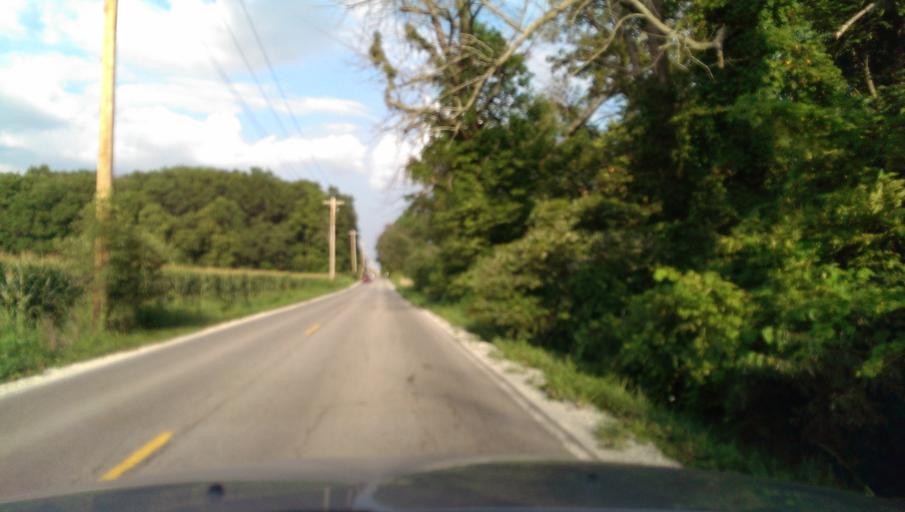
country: US
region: Indiana
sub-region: Hamilton County
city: Westfield
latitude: 40.0649
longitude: -86.1125
